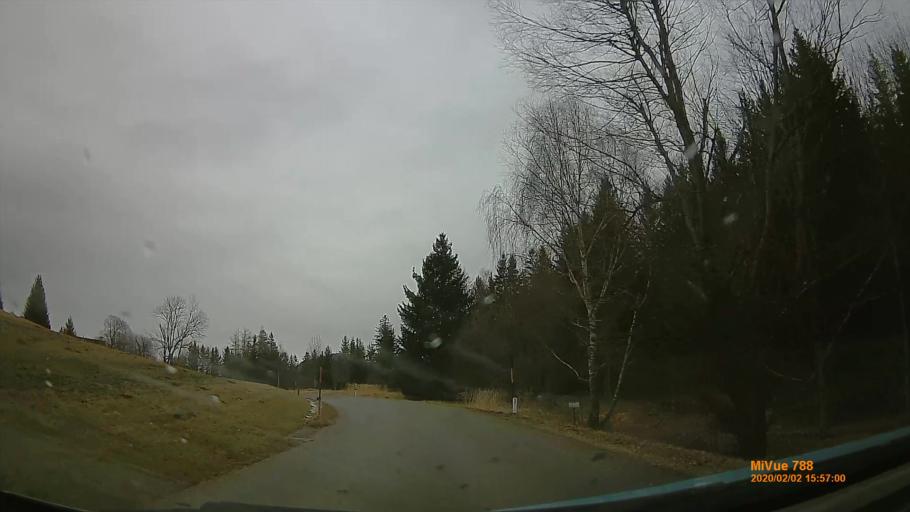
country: AT
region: Lower Austria
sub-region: Politischer Bezirk Neunkirchen
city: Semmering
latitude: 47.6638
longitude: 15.7898
